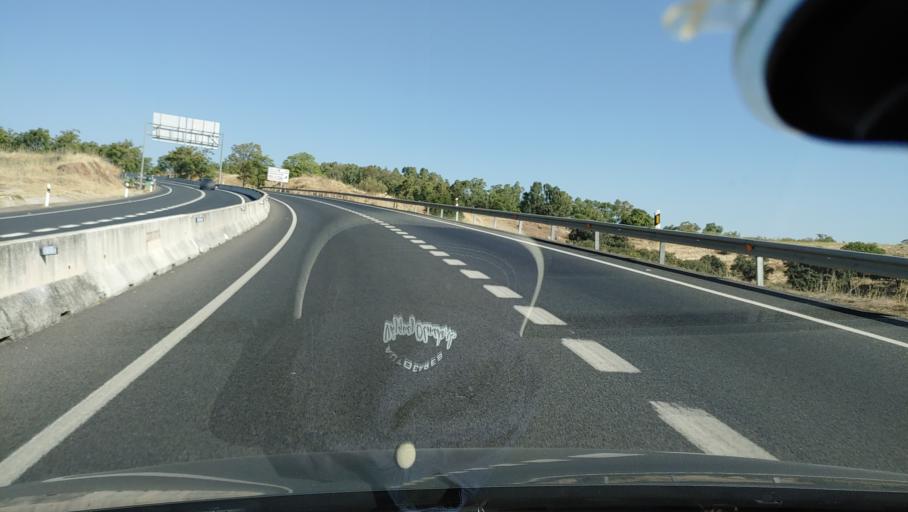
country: ES
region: Andalusia
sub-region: Province of Cordoba
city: Cordoba
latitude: 37.9116
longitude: -4.7531
